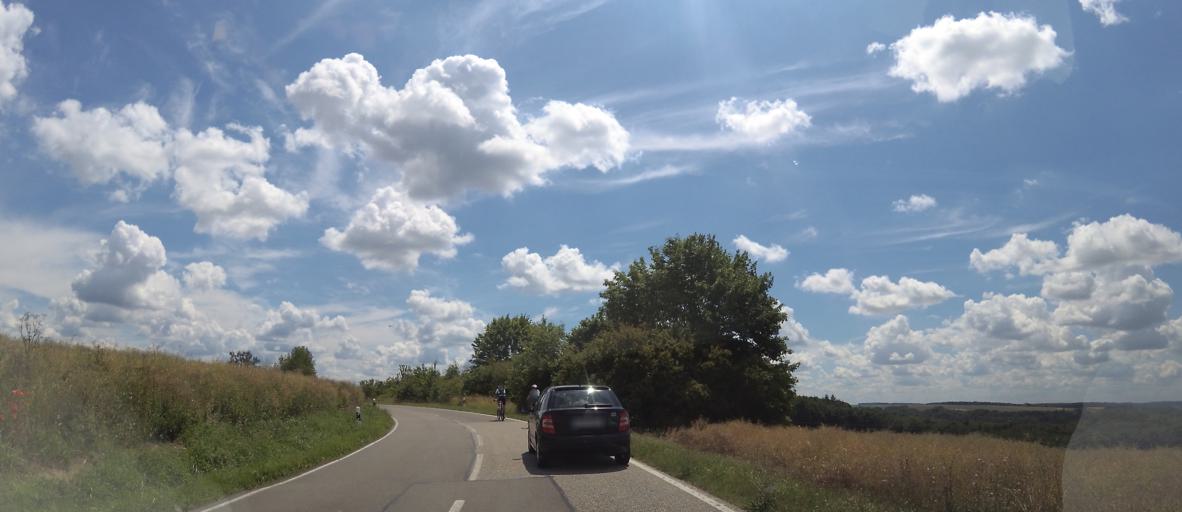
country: DE
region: Rheinland-Pfalz
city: Walshausen
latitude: 49.2173
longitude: 7.4695
